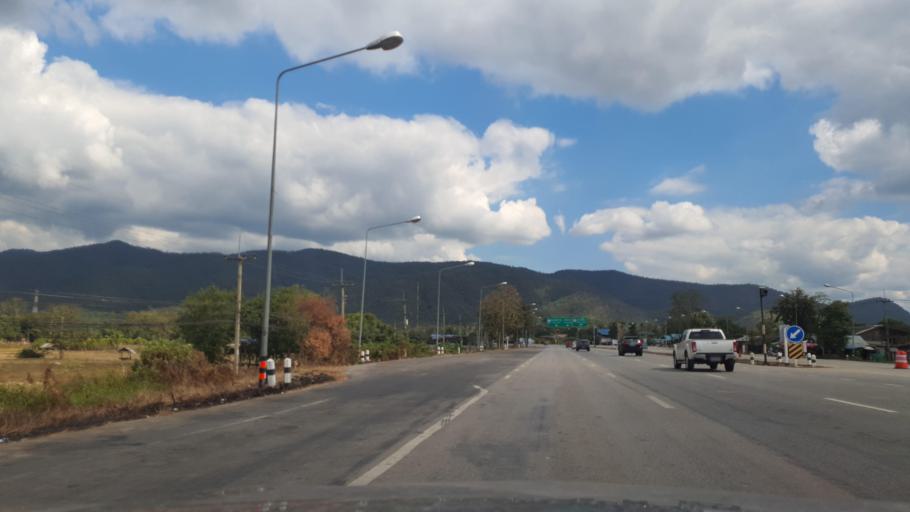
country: TH
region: Lampang
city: Thoen
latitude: 17.6494
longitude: 99.2463
